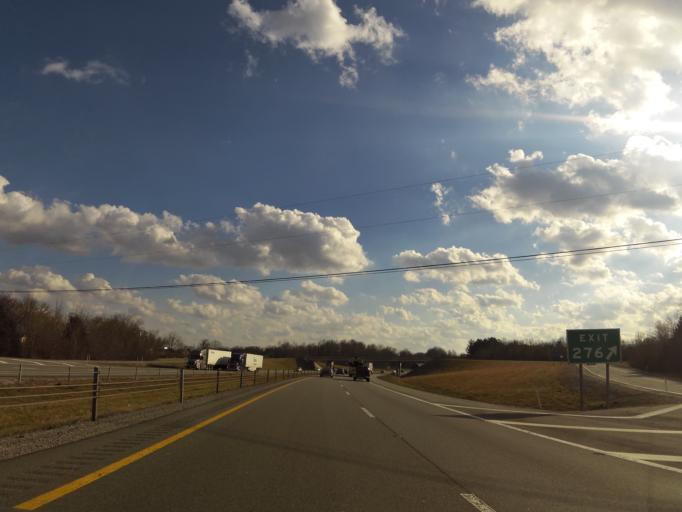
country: US
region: Tennessee
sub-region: Putnam County
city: Baxter
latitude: 36.1150
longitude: -85.6860
